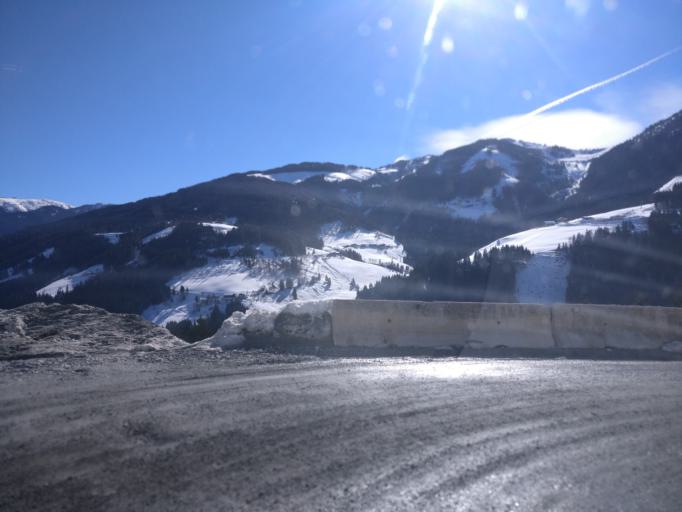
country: AT
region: Salzburg
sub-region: Politischer Bezirk Sankt Johann im Pongau
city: Sankt Johann im Pongau
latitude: 47.3365
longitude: 13.2373
